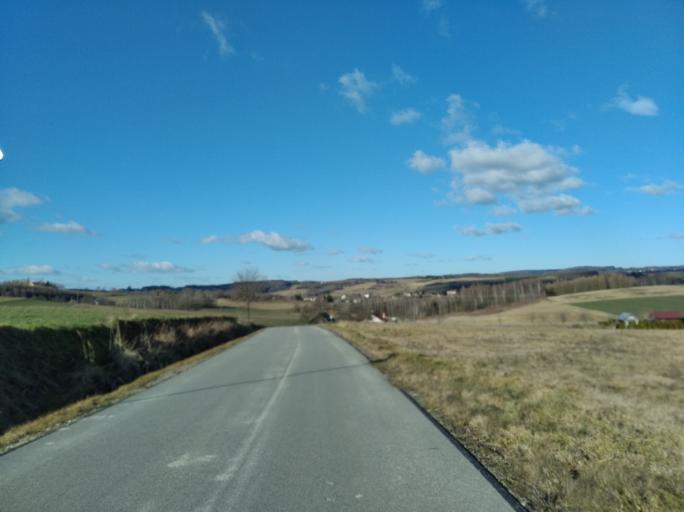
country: PL
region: Subcarpathian Voivodeship
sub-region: Powiat strzyzowski
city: Wisniowa
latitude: 49.9007
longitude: 21.6830
